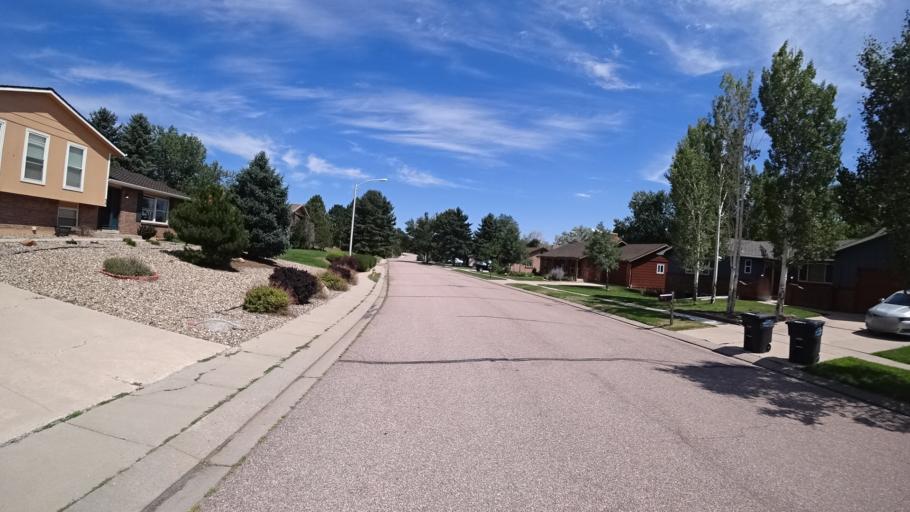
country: US
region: Colorado
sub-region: El Paso County
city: Air Force Academy
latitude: 38.9307
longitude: -104.8278
